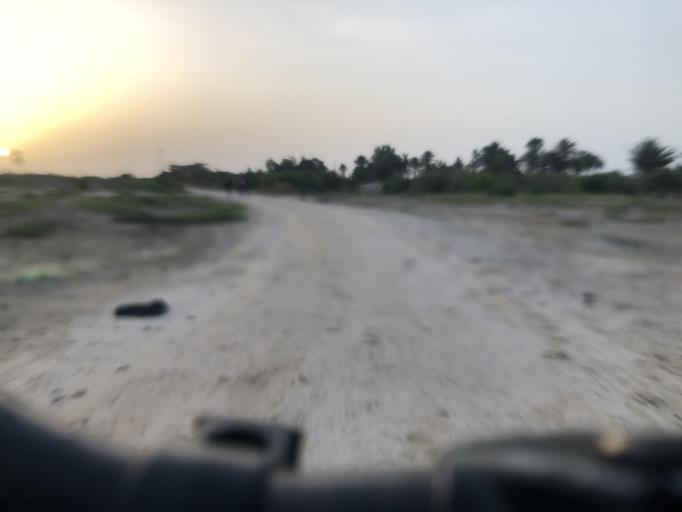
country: SN
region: Saint-Louis
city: Saint-Louis
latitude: 16.0716
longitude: -16.4318
